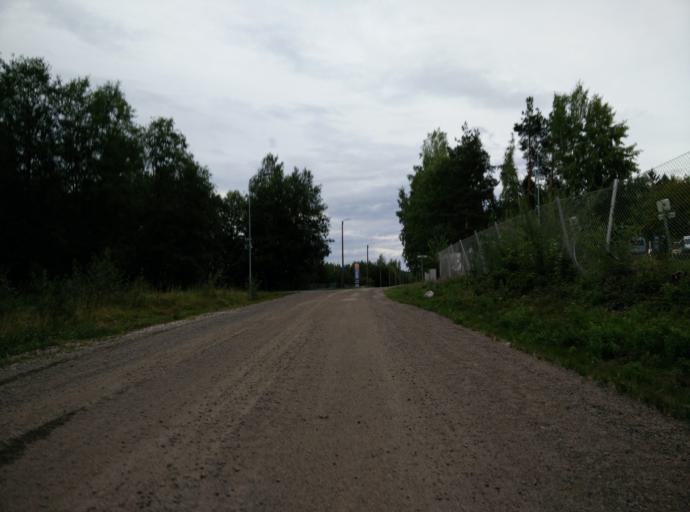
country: FI
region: Haeme
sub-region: Haemeenlinna
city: Haemeenlinna
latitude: 60.9876
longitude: 24.4813
